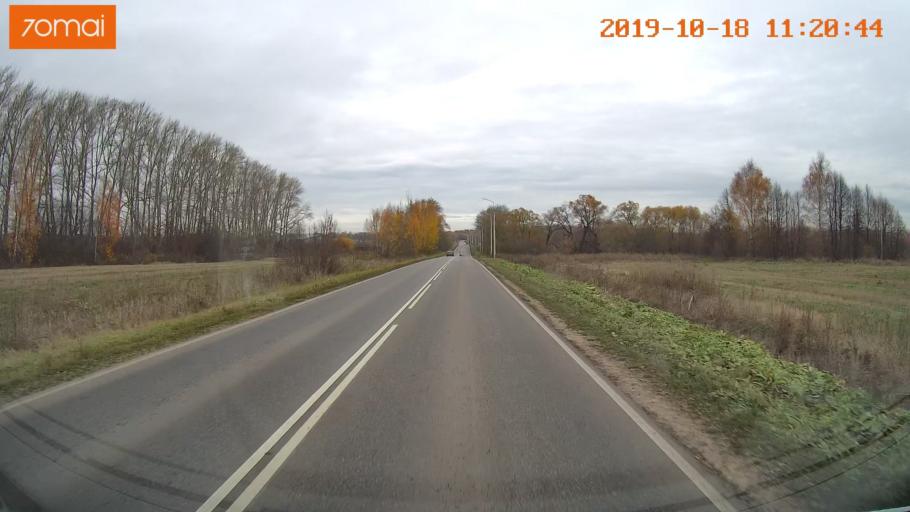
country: RU
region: Tula
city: Kimovsk
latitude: 54.0653
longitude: 38.5602
